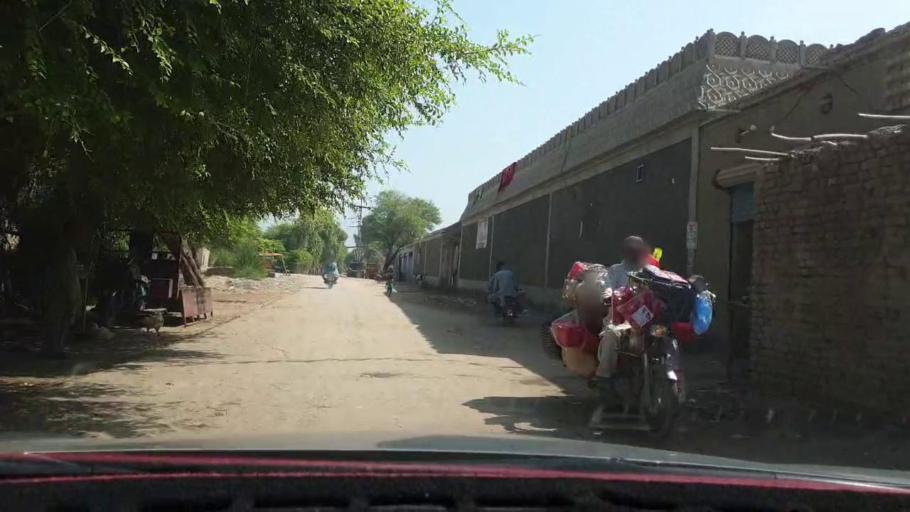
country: PK
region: Sindh
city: Warah
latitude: 27.4825
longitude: 67.8301
